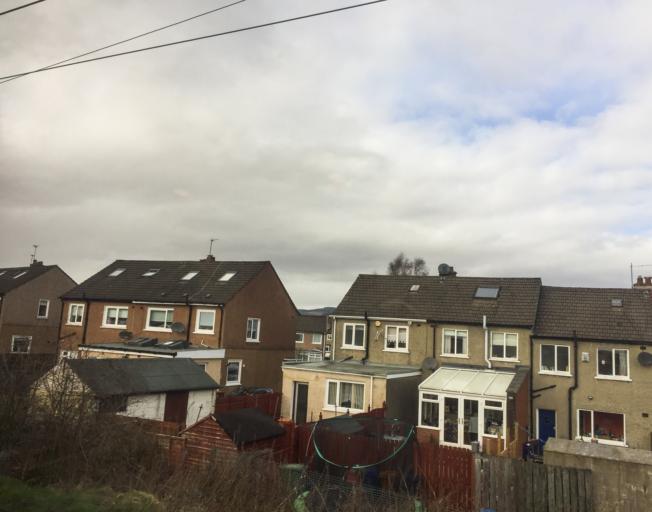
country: GB
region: Scotland
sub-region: East Dunbartonshire
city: Bearsden
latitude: 55.9065
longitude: -4.3451
